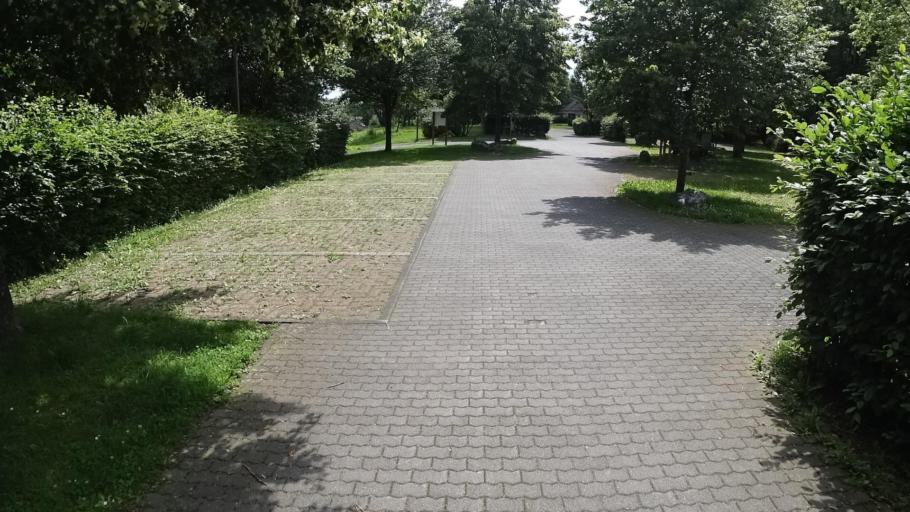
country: DE
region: Rheinland-Pfalz
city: Vettelschoss
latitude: 50.6142
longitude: 7.3358
